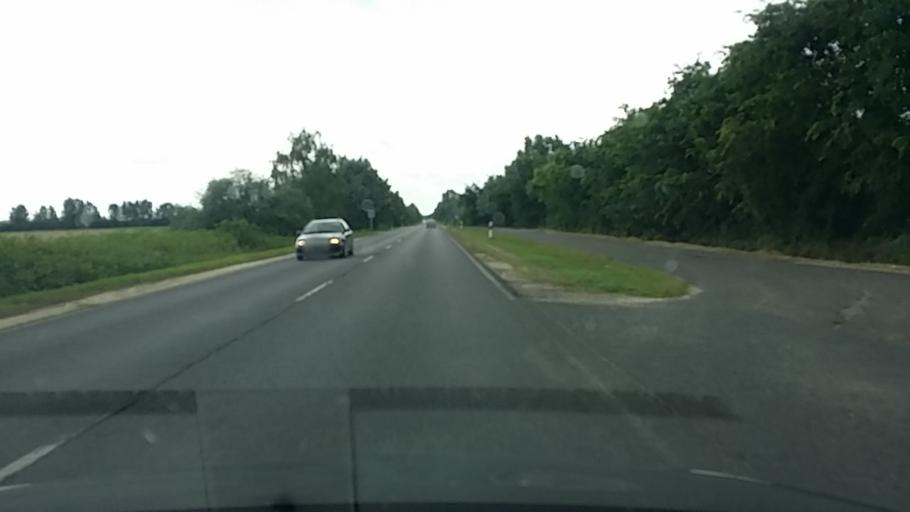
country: HU
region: Pest
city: Orkeny
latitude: 47.1123
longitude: 19.4532
